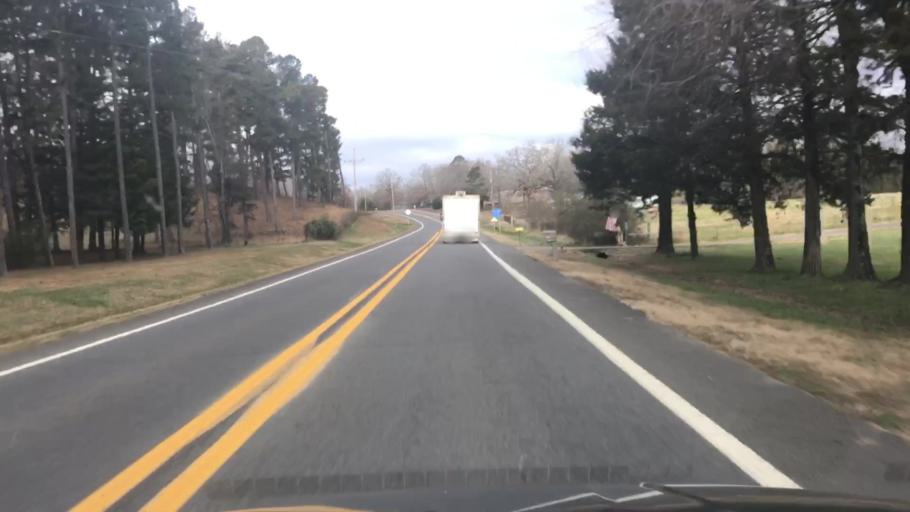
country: US
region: Arkansas
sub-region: Montgomery County
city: Mount Ida
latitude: 34.6226
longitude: -93.7253
